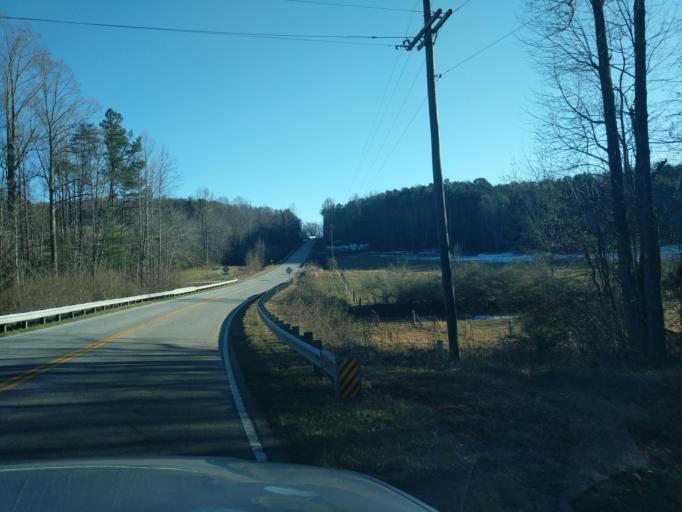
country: US
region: Georgia
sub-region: Rabun County
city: Clayton
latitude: 34.8056
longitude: -83.2758
